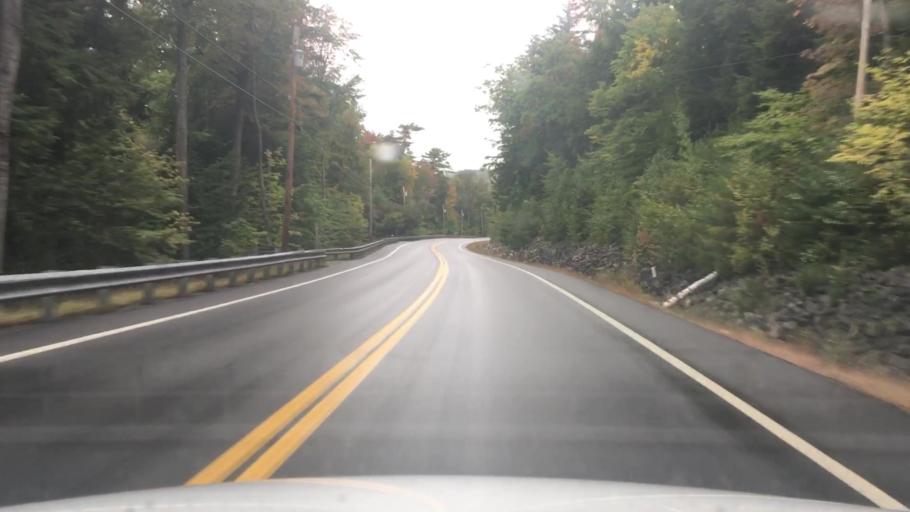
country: US
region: Maine
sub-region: Kennebec County
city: Rome
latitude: 44.5455
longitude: -69.8934
